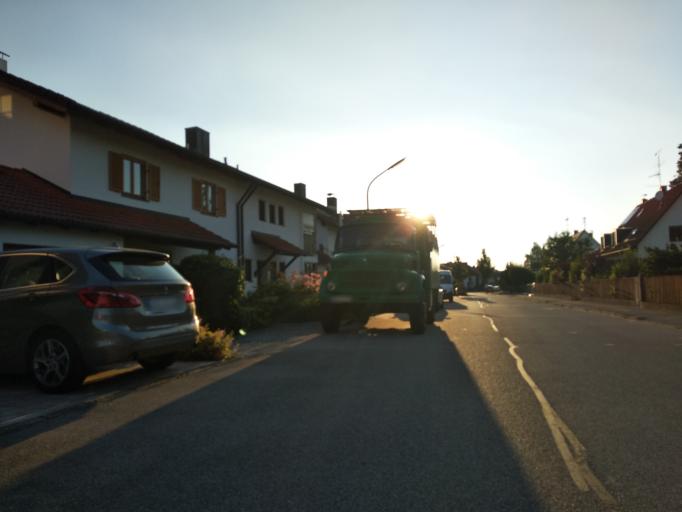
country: DE
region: Bavaria
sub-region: Upper Bavaria
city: Forstinning
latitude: 48.1676
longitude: 11.9175
